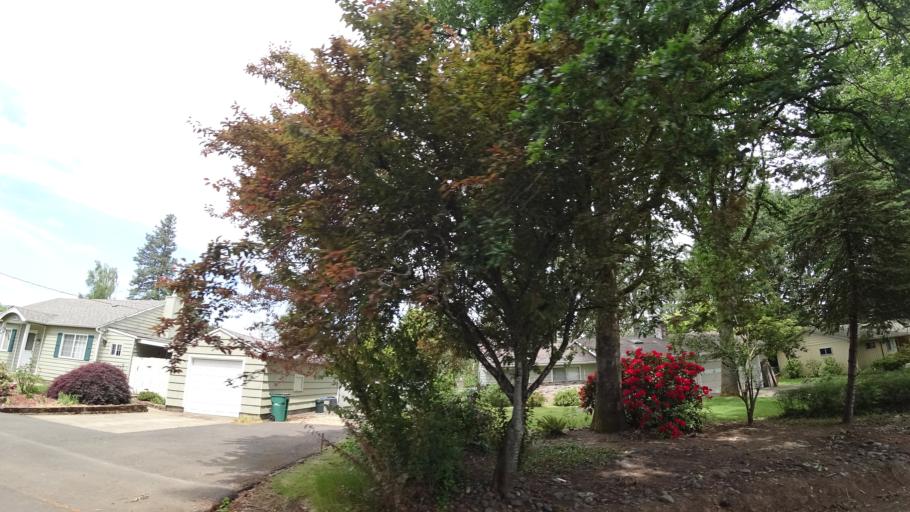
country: US
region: Oregon
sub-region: Washington County
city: Metzger
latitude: 45.4480
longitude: -122.7685
